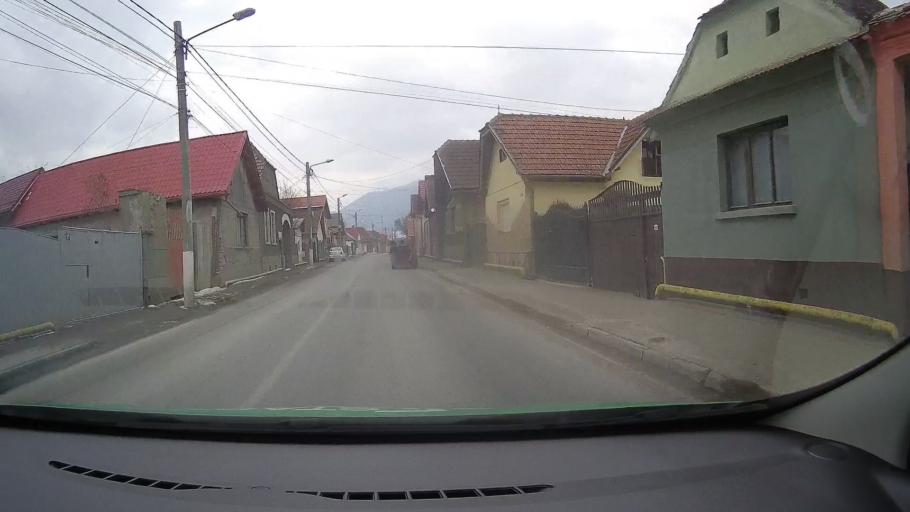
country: RO
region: Brasov
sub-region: Comuna Zarnesti
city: Tohanu Nou
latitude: 45.5724
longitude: 25.3566
